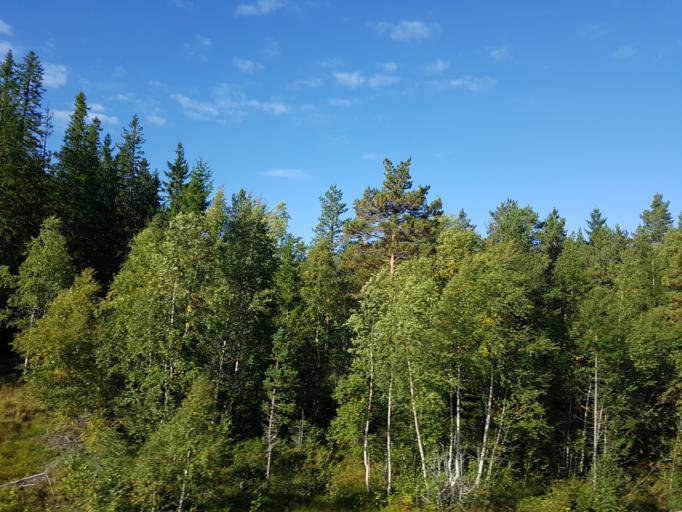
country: NO
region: Sor-Trondelag
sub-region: Trondheim
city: Trondheim
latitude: 63.6119
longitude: 10.2377
